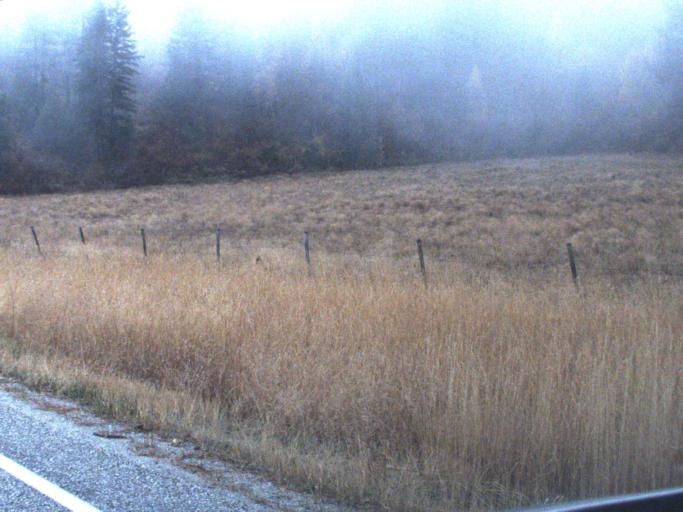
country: US
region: Washington
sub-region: Stevens County
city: Kettle Falls
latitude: 48.7622
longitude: -118.1399
